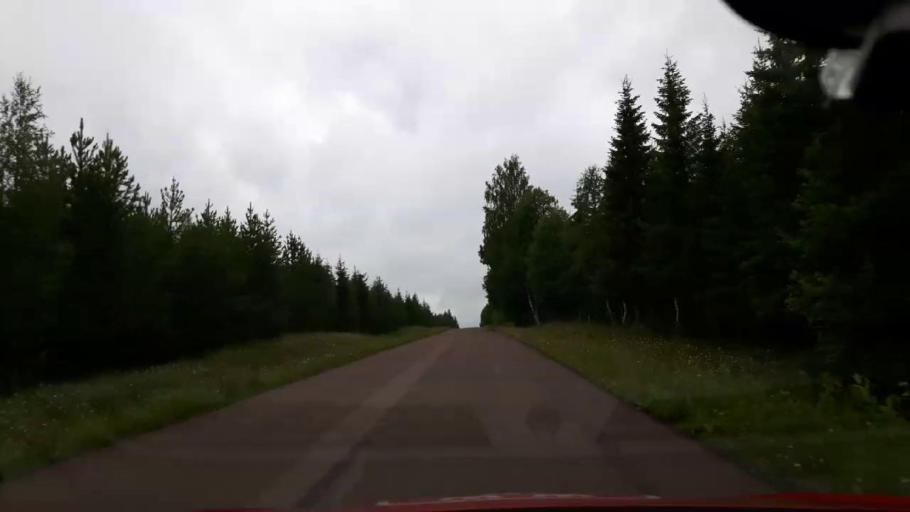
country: SE
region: Jaemtland
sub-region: Krokoms Kommun
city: Valla
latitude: 63.3689
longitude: 13.7498
